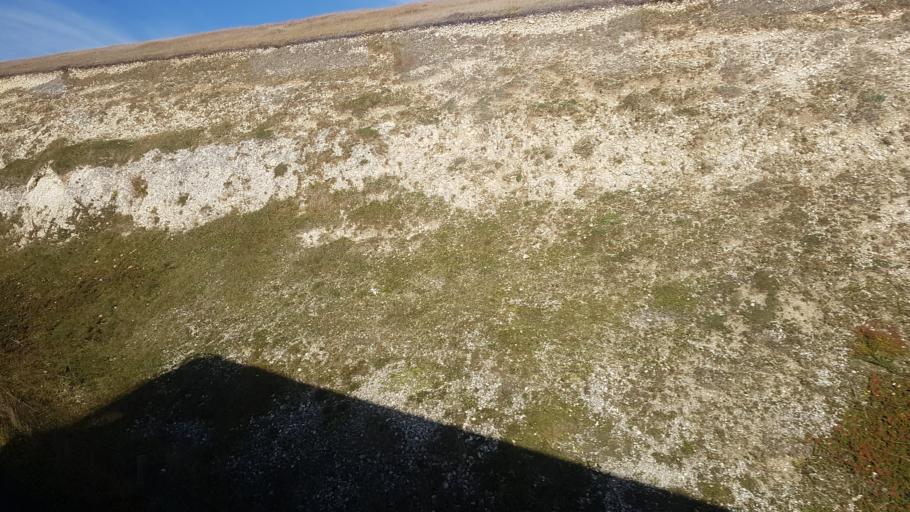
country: GB
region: England
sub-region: Isle of Wight
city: Freshwater
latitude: 50.6681
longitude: -1.4873
